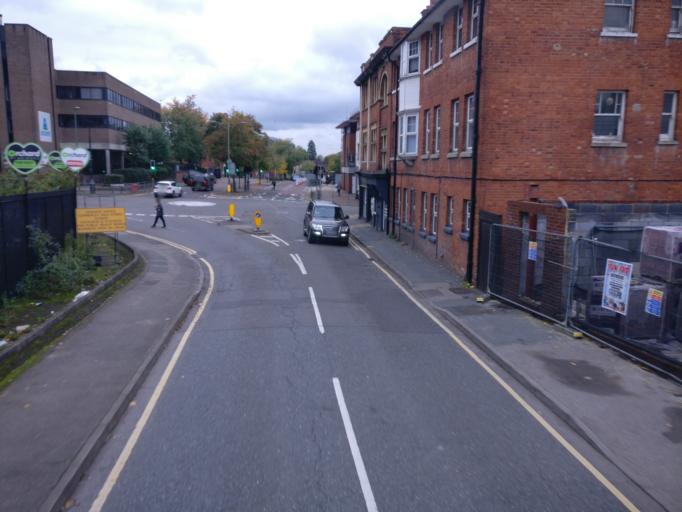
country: GB
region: England
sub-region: Surrey
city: Camberley
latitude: 51.3371
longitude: -0.7430
